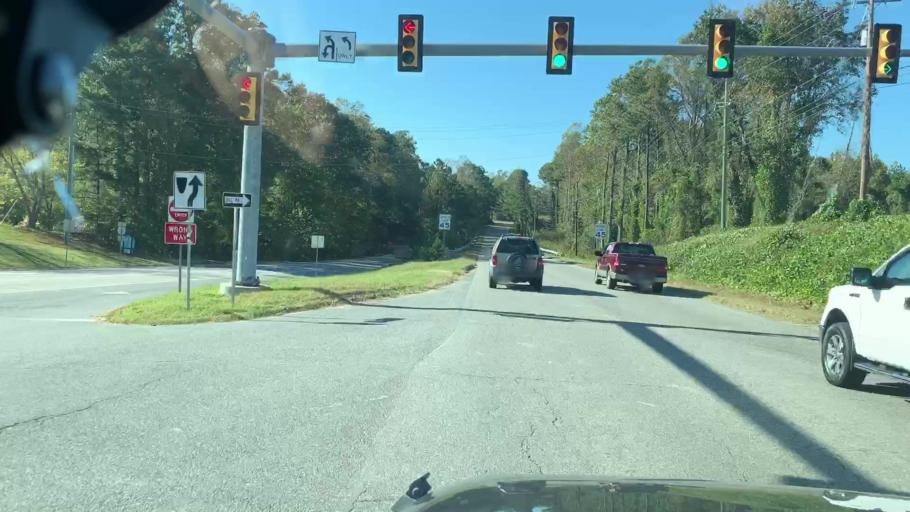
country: US
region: Virginia
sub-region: James City County
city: Williamsburg
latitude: 37.3731
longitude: -76.7780
